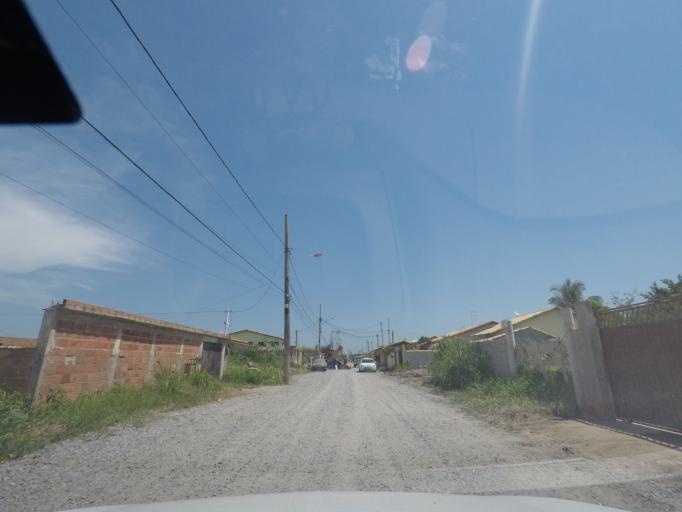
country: BR
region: Rio de Janeiro
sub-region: Marica
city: Marica
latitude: -22.9578
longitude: -42.9558
